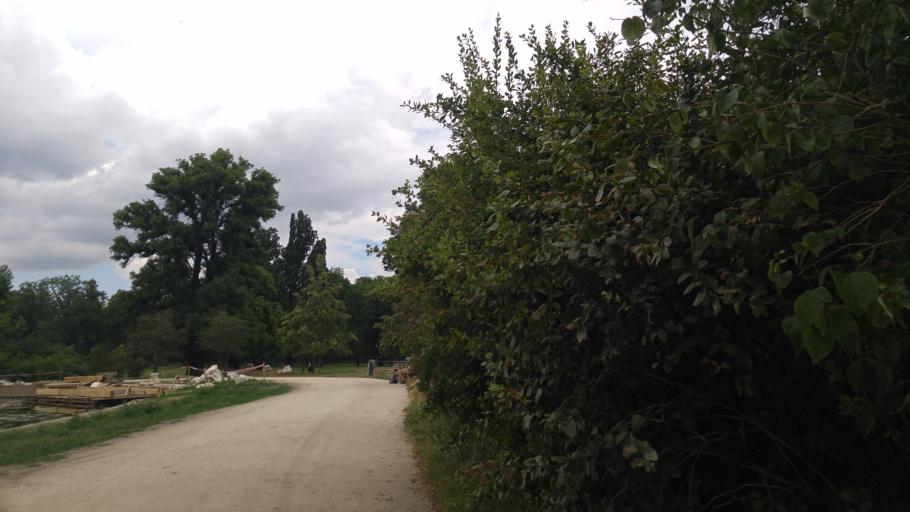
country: CZ
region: Praha
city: Prague
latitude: 50.1068
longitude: 14.4220
